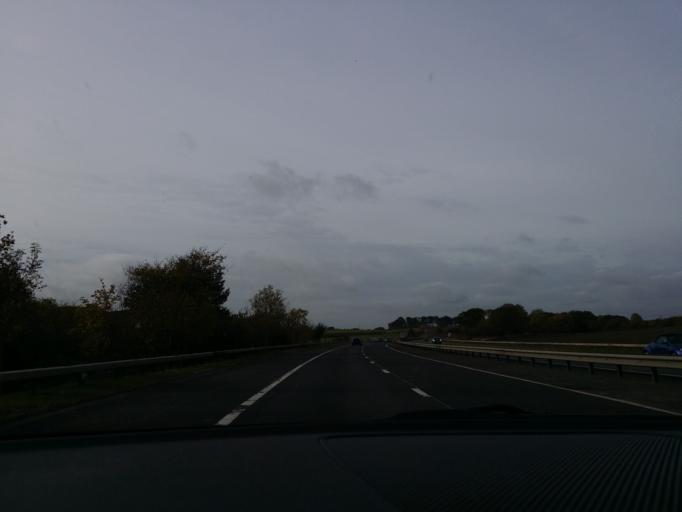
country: GB
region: Scotland
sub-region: Edinburgh
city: Kirkliston
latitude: 55.9576
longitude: -3.4333
